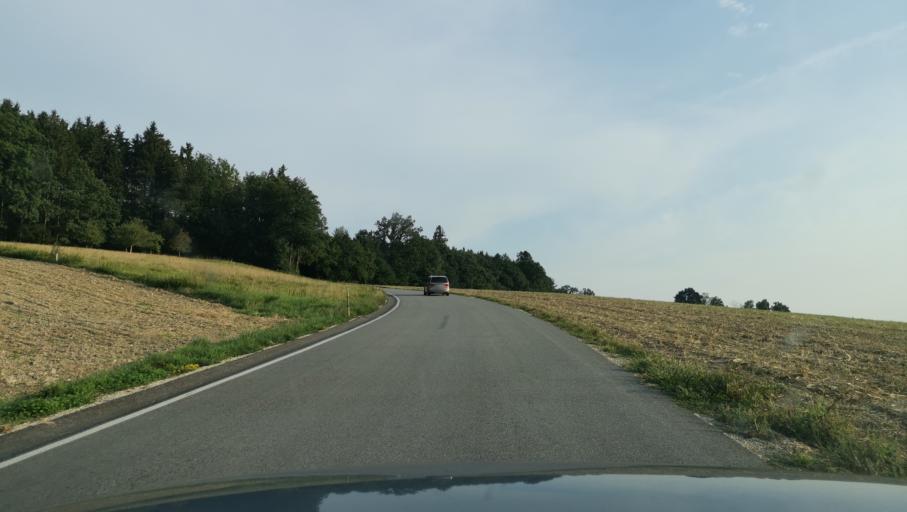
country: AT
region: Upper Austria
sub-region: Politischer Bezirk Grieskirchen
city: Grieskirchen
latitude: 48.3038
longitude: 13.7930
